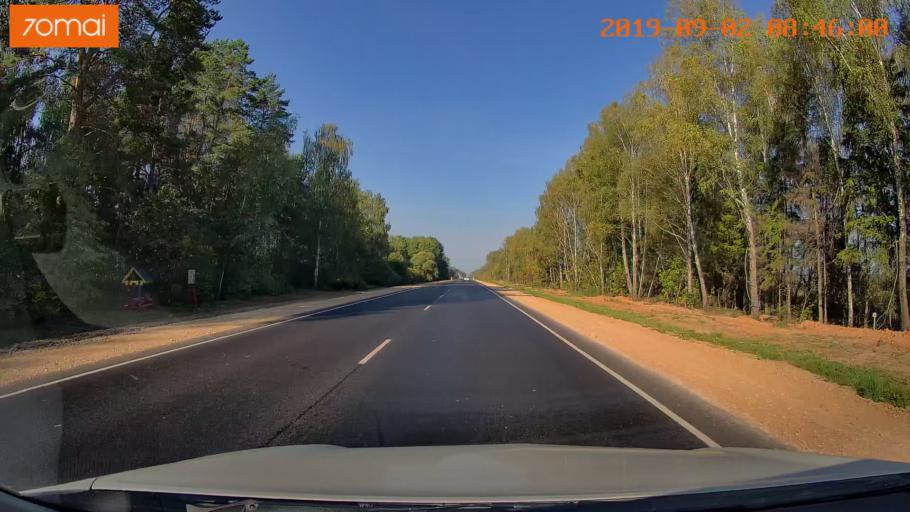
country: RU
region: Kaluga
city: Medyn'
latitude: 54.9691
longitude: 35.9898
